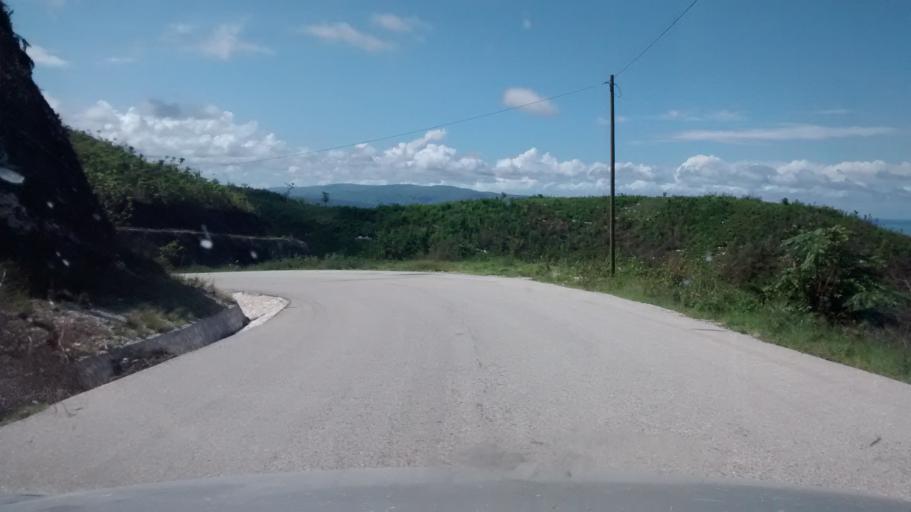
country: HT
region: Grandans
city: Corail
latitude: 18.5858
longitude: -74.0059
